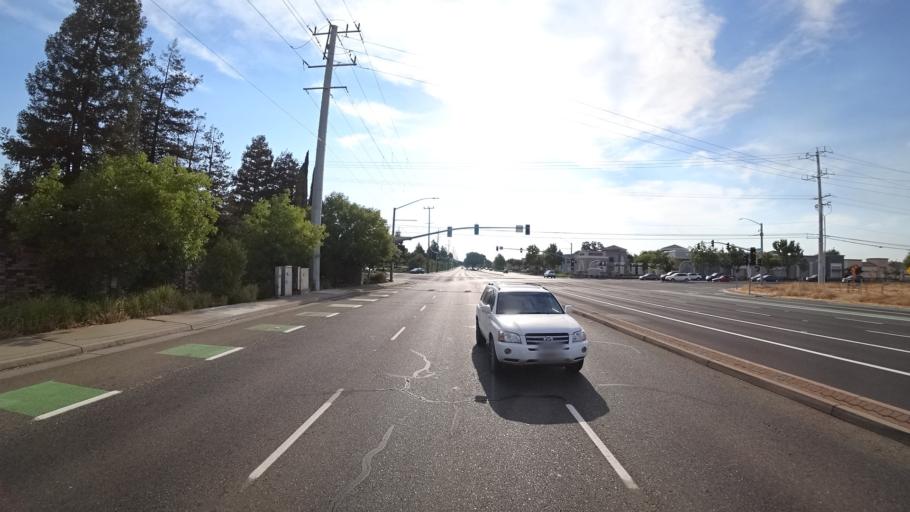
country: US
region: California
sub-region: Sacramento County
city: Laguna
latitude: 38.4087
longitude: -121.4507
